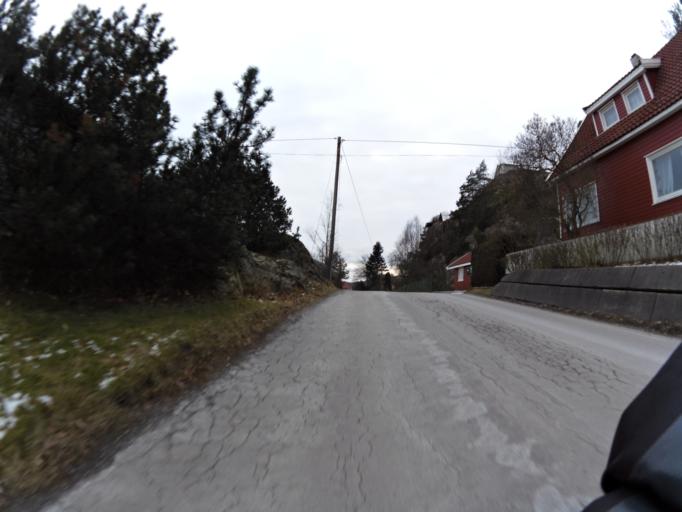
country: NO
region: Ostfold
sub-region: Fredrikstad
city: Fredrikstad
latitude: 59.2247
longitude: 10.8974
